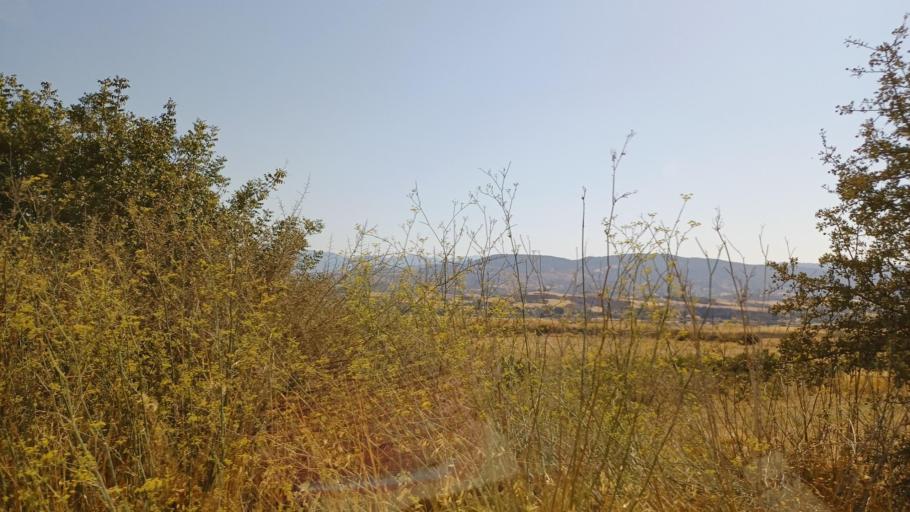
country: CY
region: Pafos
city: Polis
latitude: 35.0122
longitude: 32.4189
